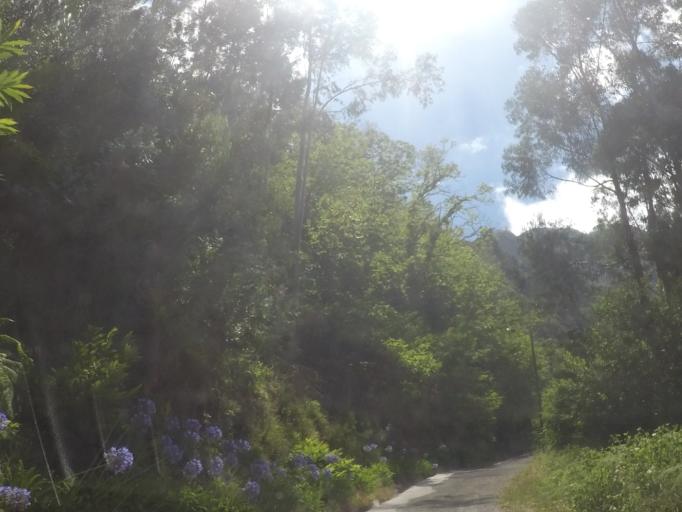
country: PT
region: Madeira
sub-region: Camara de Lobos
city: Curral das Freiras
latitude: 32.7150
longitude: -16.9744
